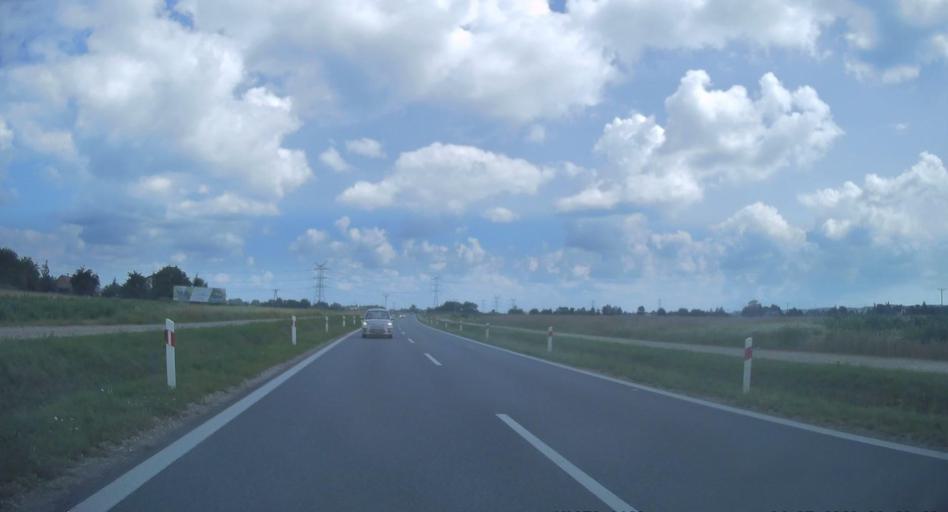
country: PL
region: Lesser Poland Voivodeship
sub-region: Powiat tarnowski
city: Wojnicz
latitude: 49.9405
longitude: 20.8450
